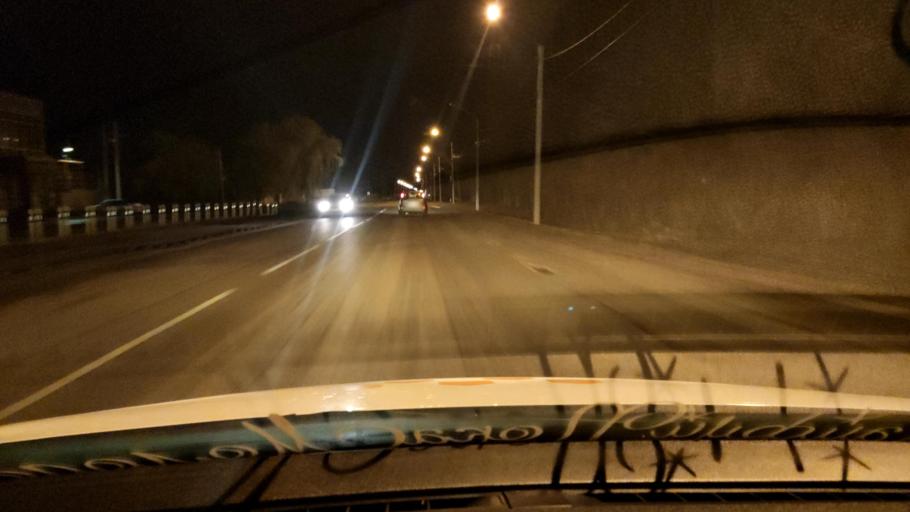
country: RU
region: Voronezj
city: Semiluki
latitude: 51.7022
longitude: 39.0178
